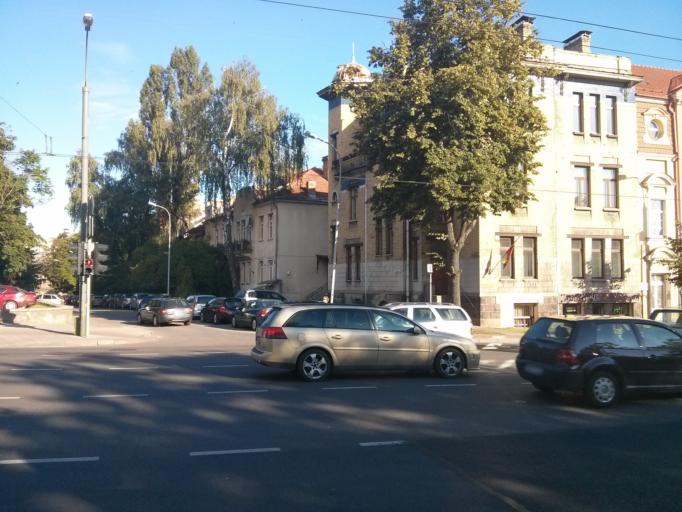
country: LT
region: Vilnius County
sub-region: Vilnius
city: Vilnius
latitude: 54.6906
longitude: 25.2700
